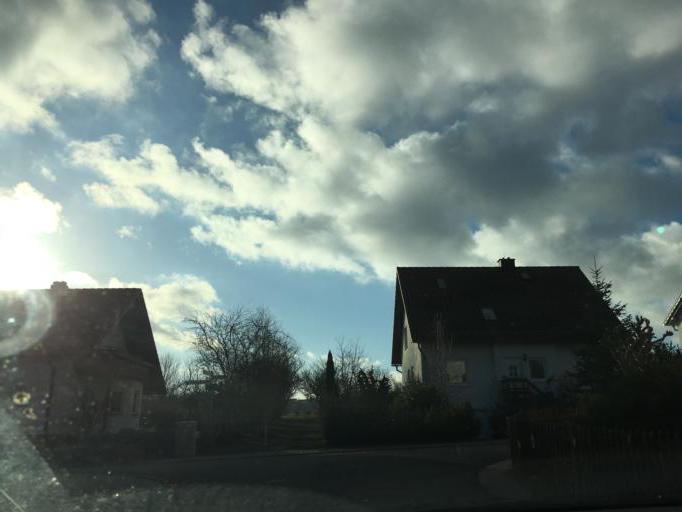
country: DE
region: Thuringia
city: Bad Berka
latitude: 50.9020
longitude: 11.2716
